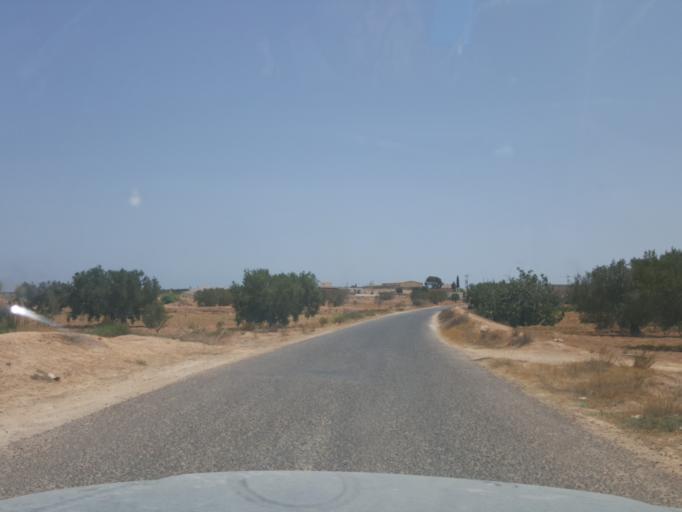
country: TN
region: Qabis
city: Gabes
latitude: 34.0553
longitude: 9.9817
